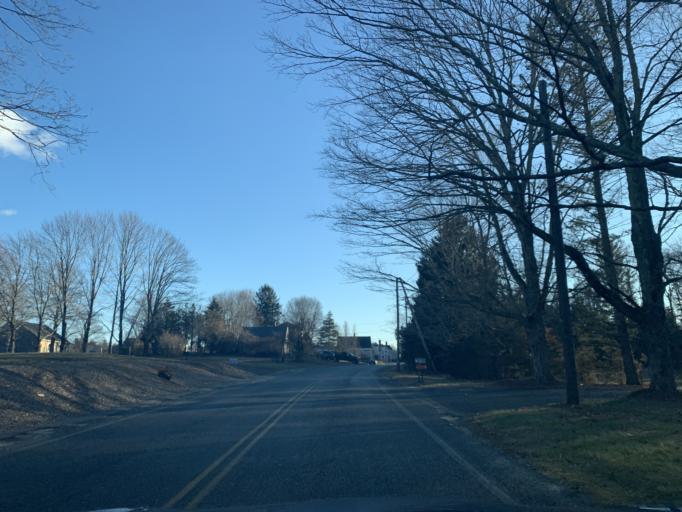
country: US
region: Massachusetts
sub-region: Bristol County
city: Norton
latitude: 41.9044
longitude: -71.2022
